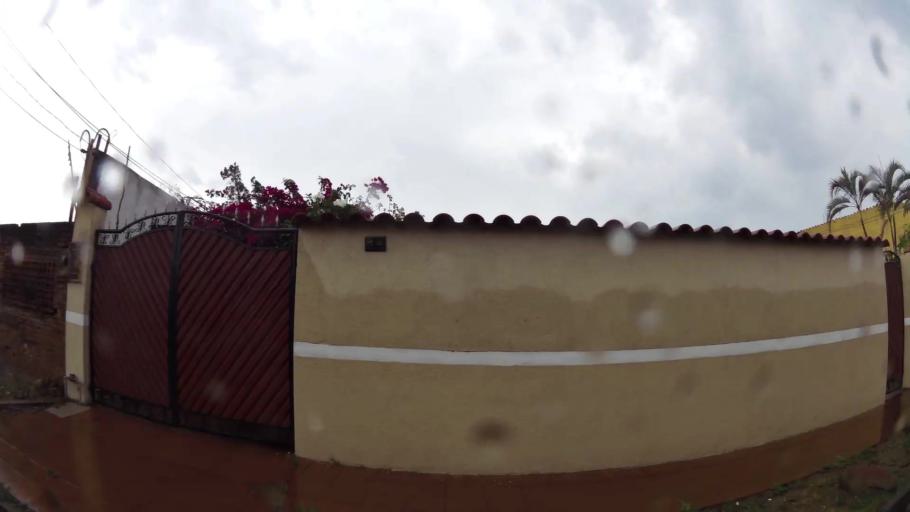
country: BO
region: Santa Cruz
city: Santa Cruz de la Sierra
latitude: -17.7930
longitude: -63.1536
